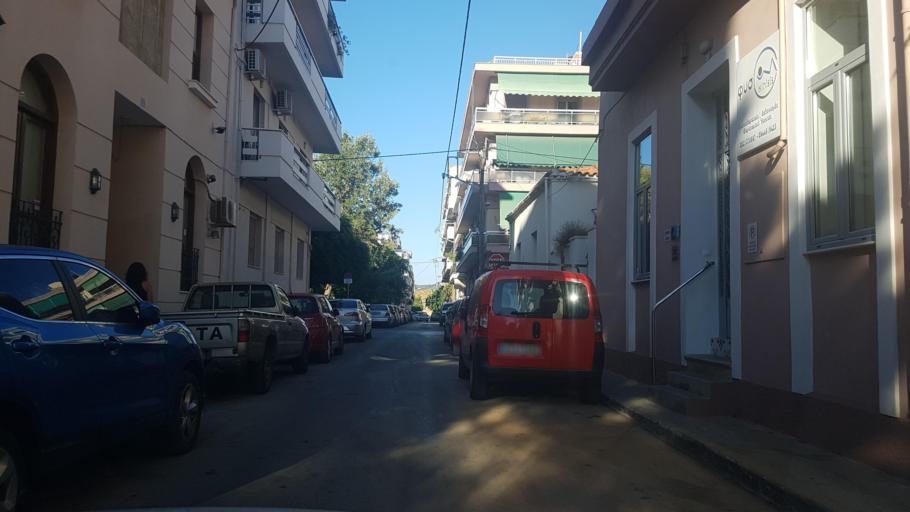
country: GR
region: Crete
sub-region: Nomos Chanias
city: Chania
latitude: 35.5139
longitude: 24.0123
